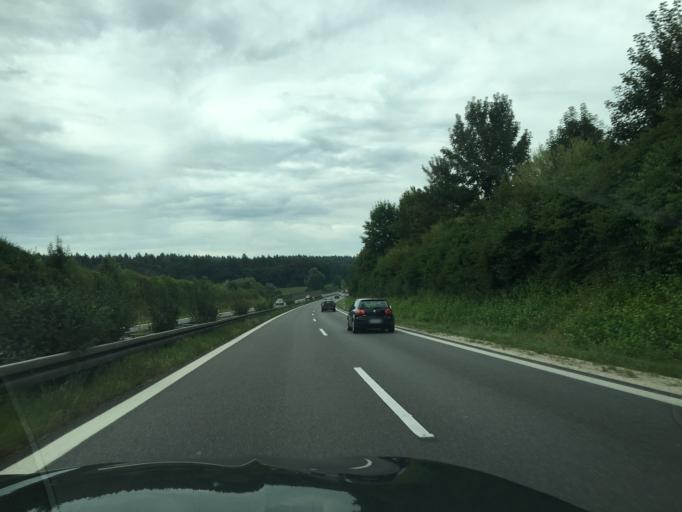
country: DE
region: Baden-Wuerttemberg
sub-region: Freiburg Region
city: Radolfzell am Bodensee
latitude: 47.7482
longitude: 9.0095
